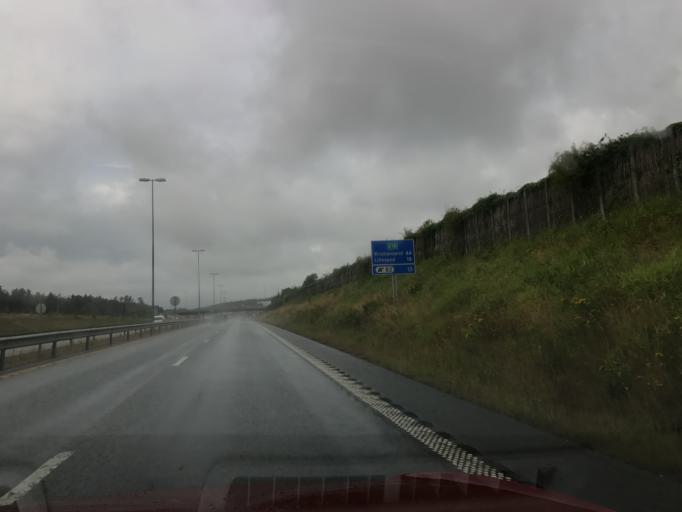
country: NO
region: Aust-Agder
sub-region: Grimstad
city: Grimstad
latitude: 58.3392
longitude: 8.5609
